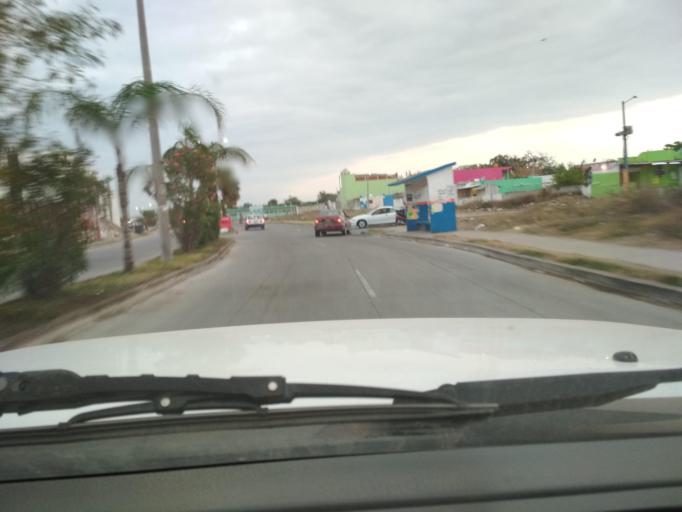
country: MX
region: Veracruz
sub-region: Medellin
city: Fraccionamiento Arboledas San Ramon
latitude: 19.0973
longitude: -96.1628
